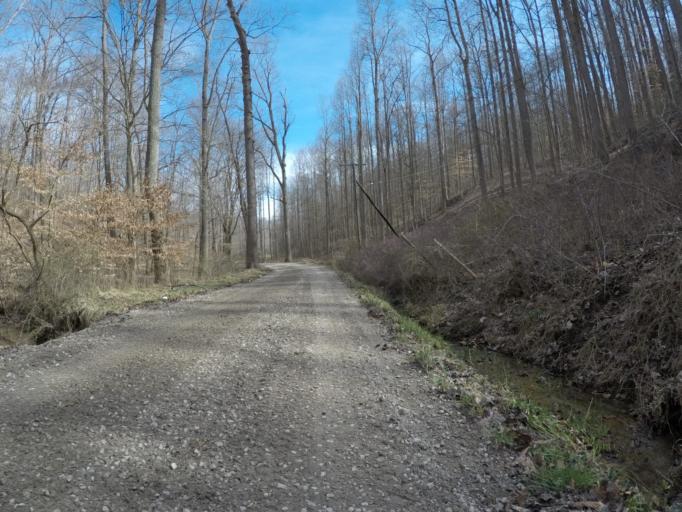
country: US
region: West Virginia
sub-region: Wayne County
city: Ceredo
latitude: 38.3446
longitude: -82.5455
